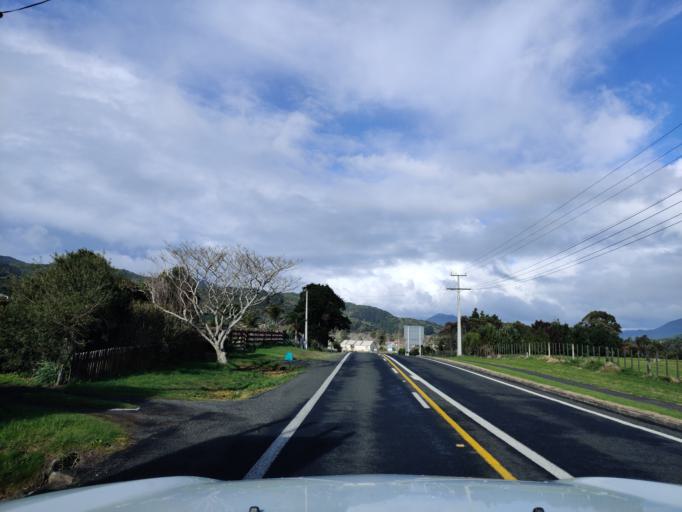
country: NZ
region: Waikato
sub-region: Thames-Coromandel District
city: Coromandel
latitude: -36.7637
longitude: 175.5017
